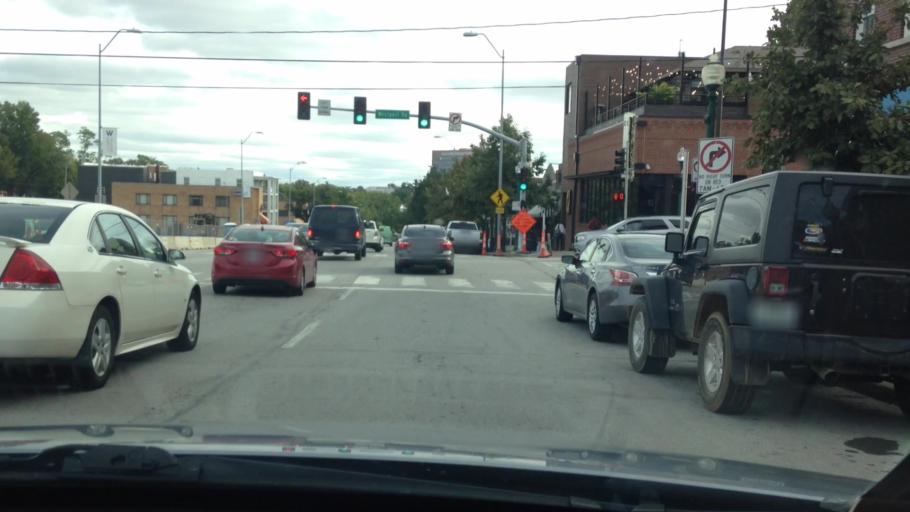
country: US
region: Kansas
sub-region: Johnson County
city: Westwood
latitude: 39.0535
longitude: -94.5908
